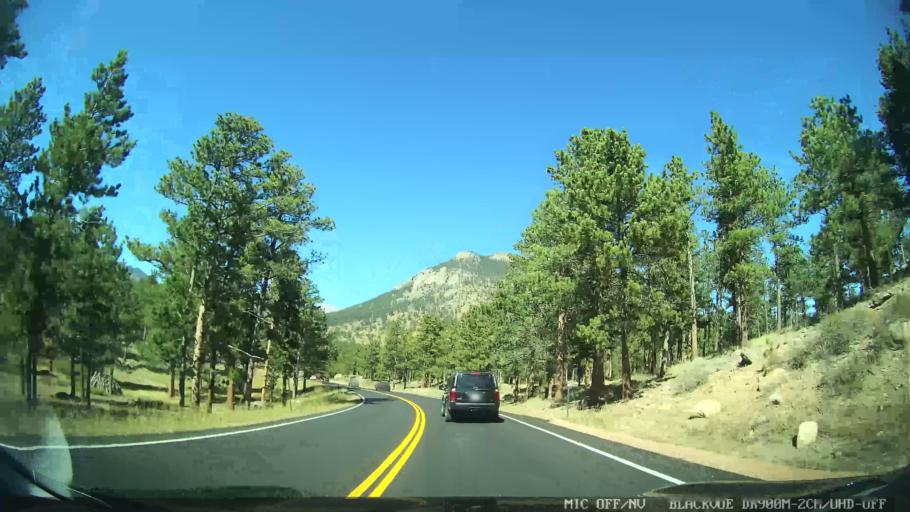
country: US
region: Colorado
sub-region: Larimer County
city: Estes Park
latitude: 40.3608
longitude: -105.5815
